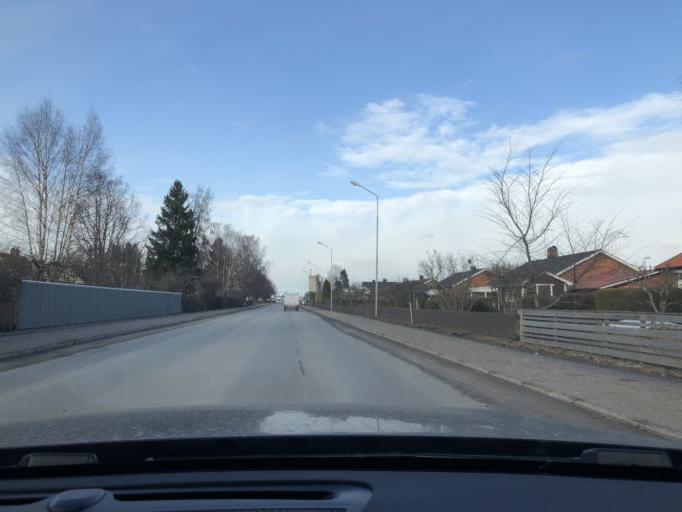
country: SE
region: Uppsala
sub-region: Tierps Kommun
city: Tierp
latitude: 60.3344
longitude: 17.5138
